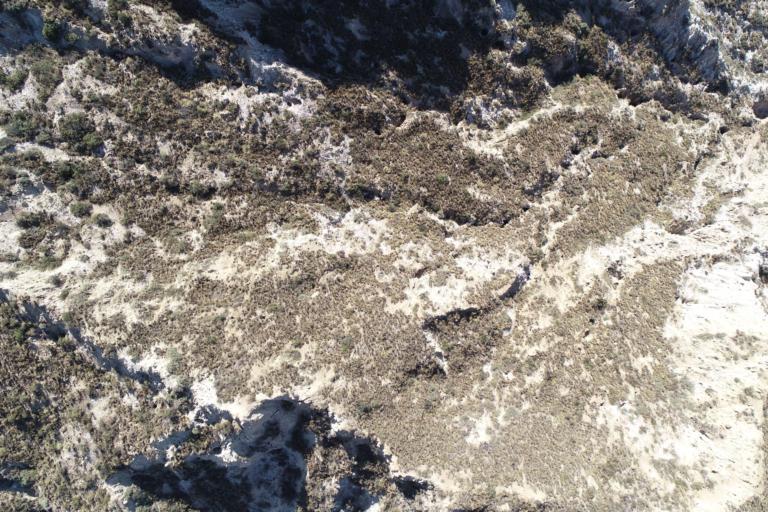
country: BO
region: La Paz
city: La Paz
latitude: -16.5509
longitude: -68.1087
